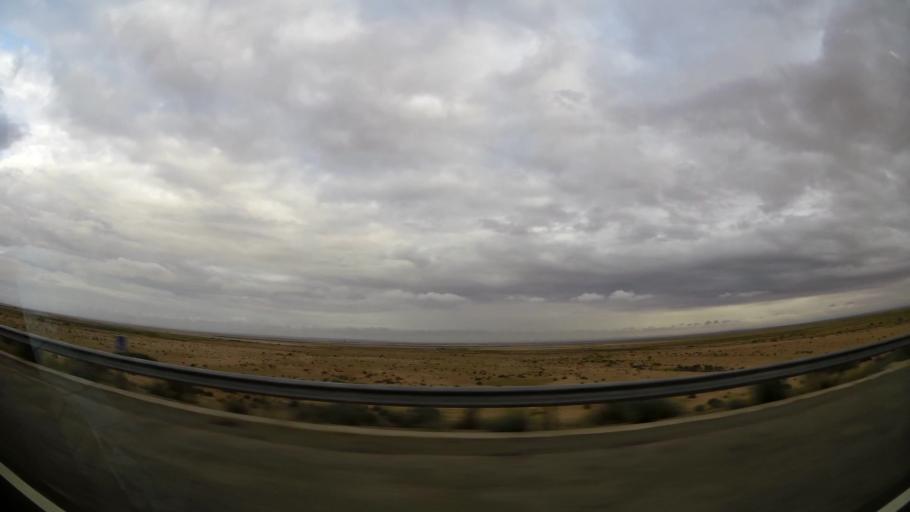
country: MA
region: Taza-Al Hoceima-Taounate
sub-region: Taza
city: Guercif
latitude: 34.3214
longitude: -3.5759
